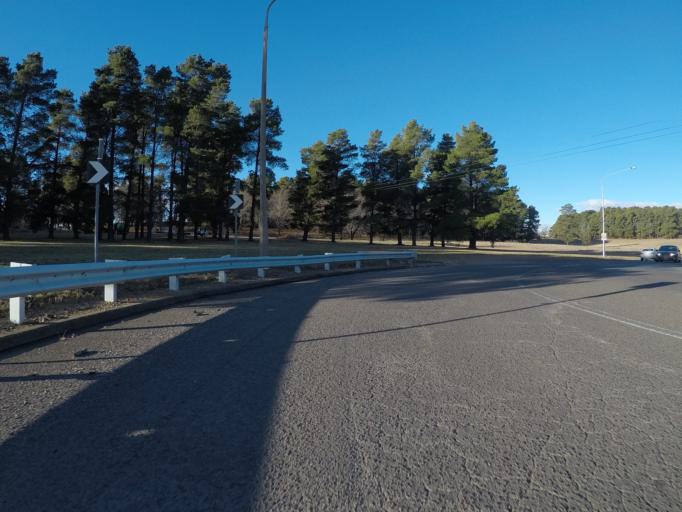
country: AU
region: Australian Capital Territory
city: Forrest
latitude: -35.3126
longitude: 149.0907
